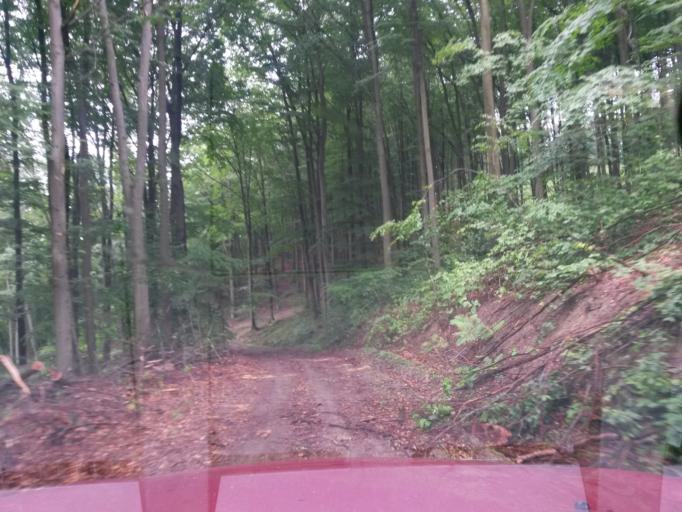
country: SK
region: Kosicky
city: Kosice
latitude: 48.7228
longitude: 21.1637
